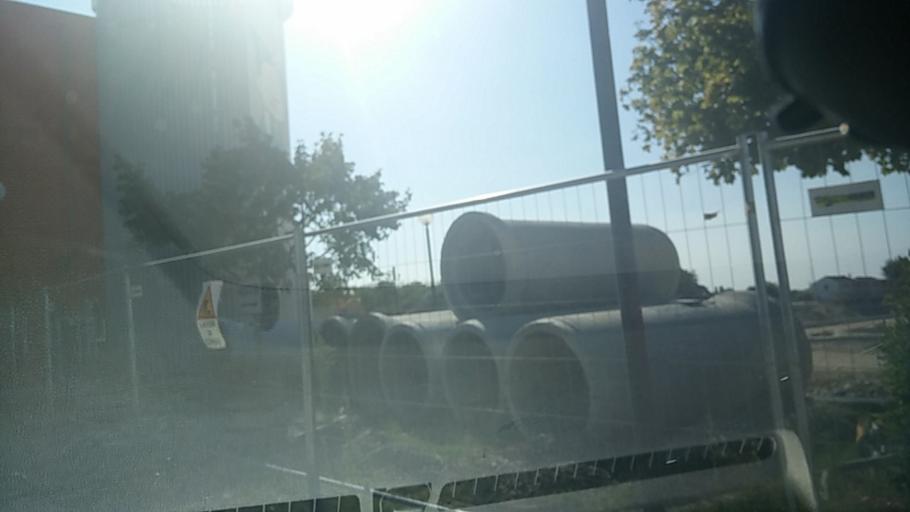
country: IT
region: Veneto
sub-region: Provincia di Venezia
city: San Dona di Piave
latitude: 45.6425
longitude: 12.5959
